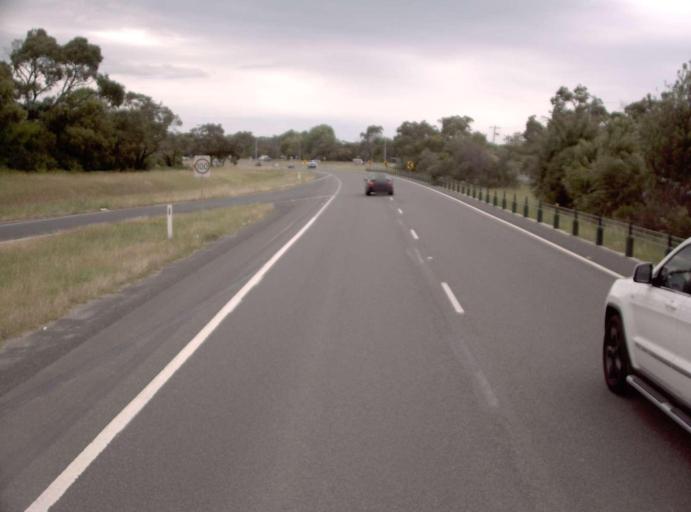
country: AU
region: Victoria
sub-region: Casey
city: Junction Village
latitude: -38.1264
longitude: 145.2902
